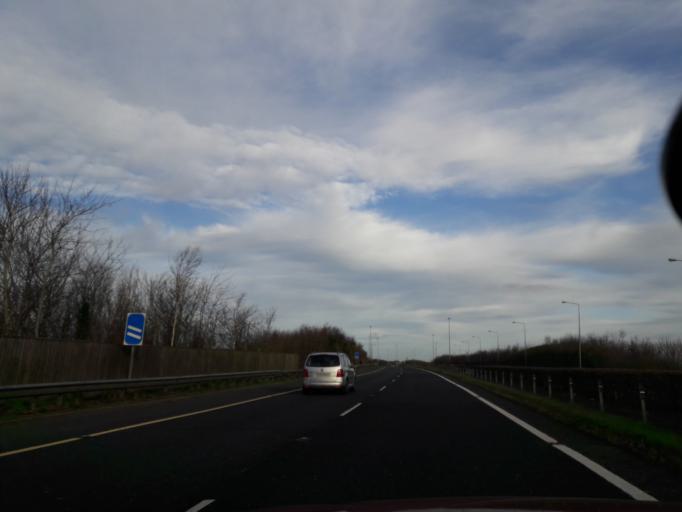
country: IE
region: Leinster
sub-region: Lu
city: Dromiskin
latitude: 53.9614
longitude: -6.4203
